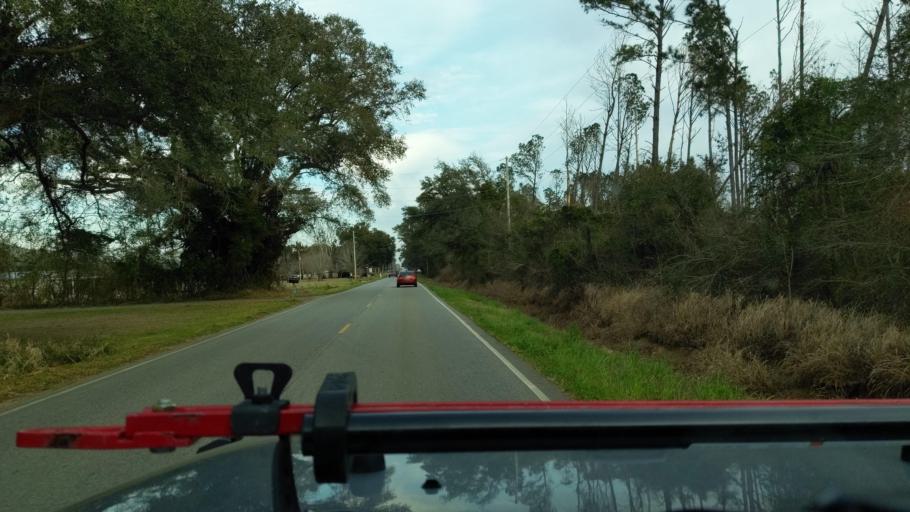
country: US
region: Alabama
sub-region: Baldwin County
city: Foley
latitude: 30.4579
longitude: -87.7704
